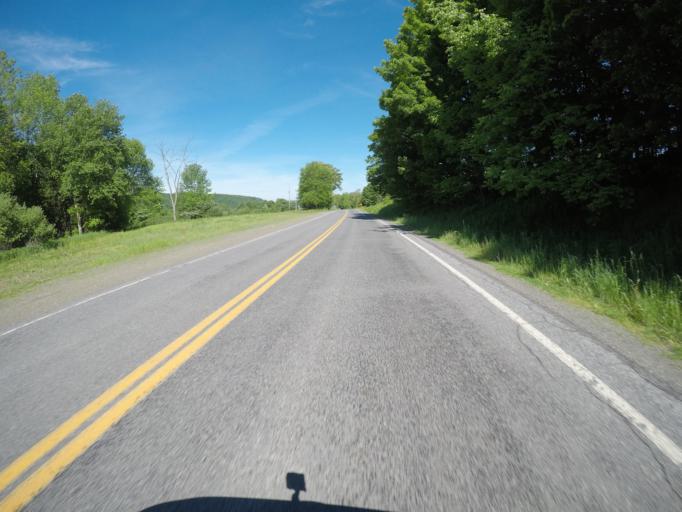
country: US
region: New York
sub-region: Delaware County
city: Delhi
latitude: 42.2076
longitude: -74.8537
